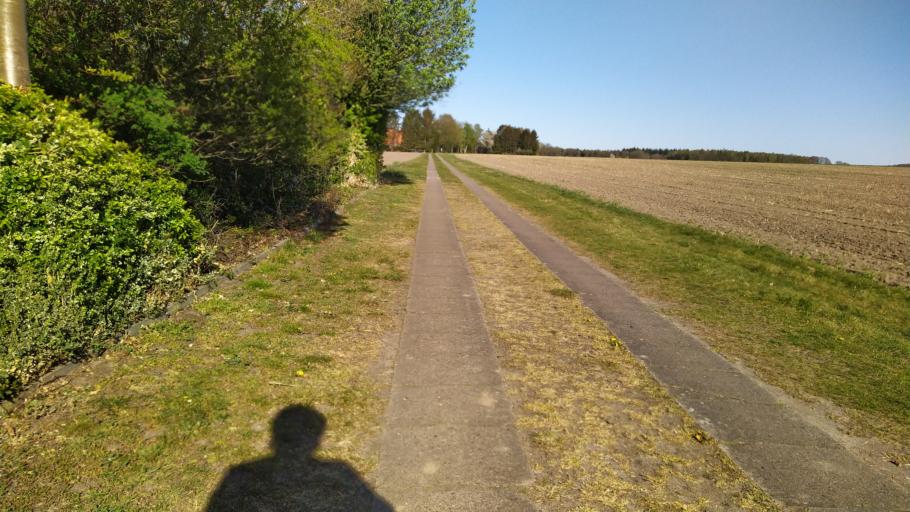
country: DE
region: Lower Saxony
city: Klein Meckelsen
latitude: 53.2939
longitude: 9.4501
